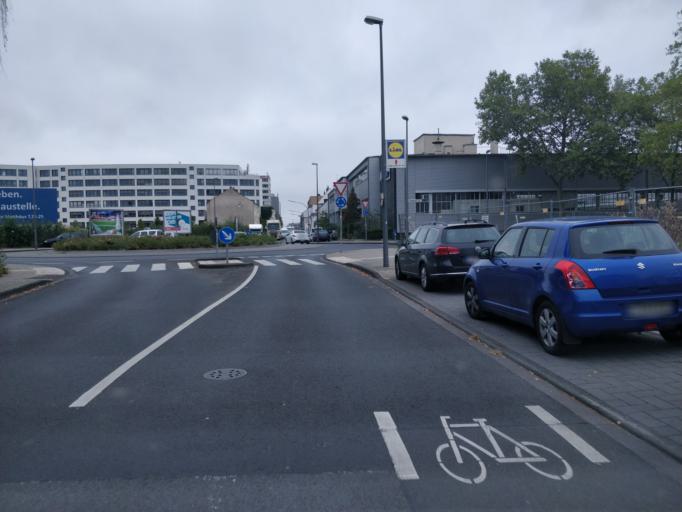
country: DE
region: North Rhine-Westphalia
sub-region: Regierungsbezirk Koln
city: Mengenich
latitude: 50.9419
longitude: 6.8895
